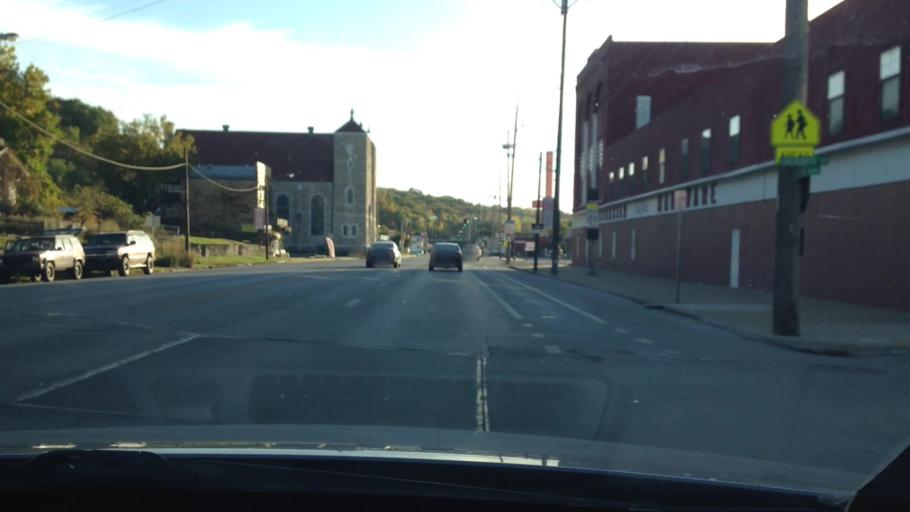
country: US
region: Kansas
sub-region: Johnson County
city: Westwood
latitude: 39.0625
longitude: -94.6197
